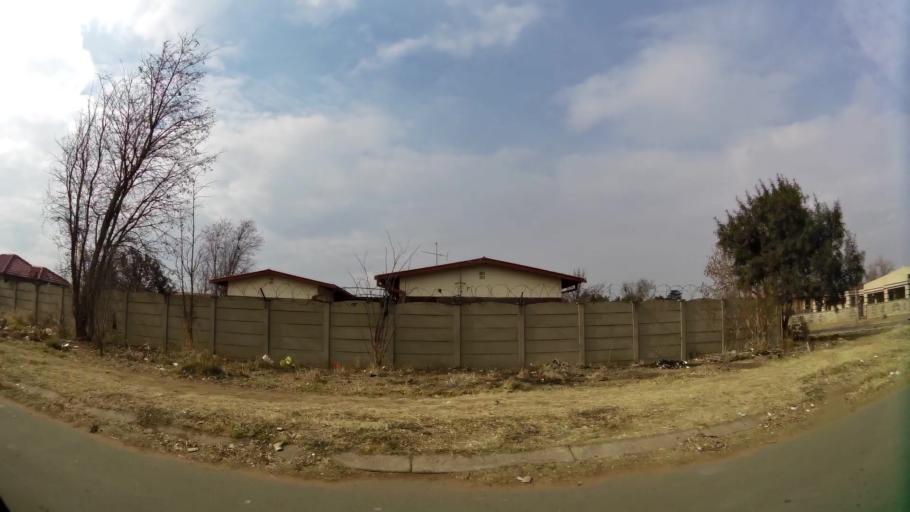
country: ZA
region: Gauteng
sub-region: Sedibeng District Municipality
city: Vanderbijlpark
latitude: -26.6850
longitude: 27.8414
